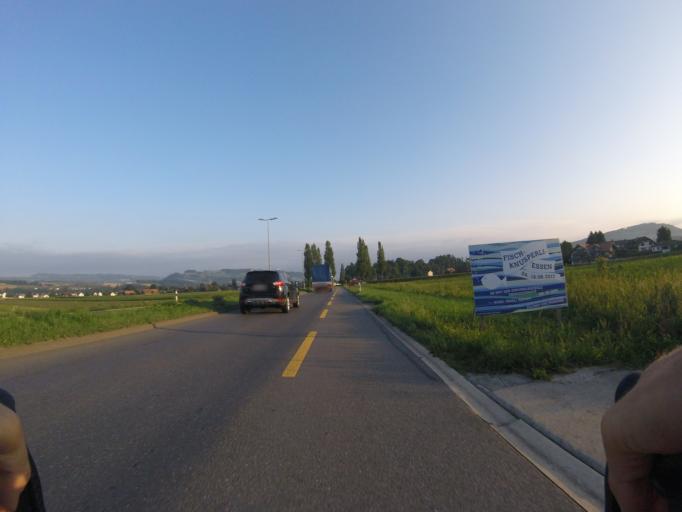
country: CH
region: Bern
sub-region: Thun District
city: Uttigen
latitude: 46.8154
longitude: 7.5907
